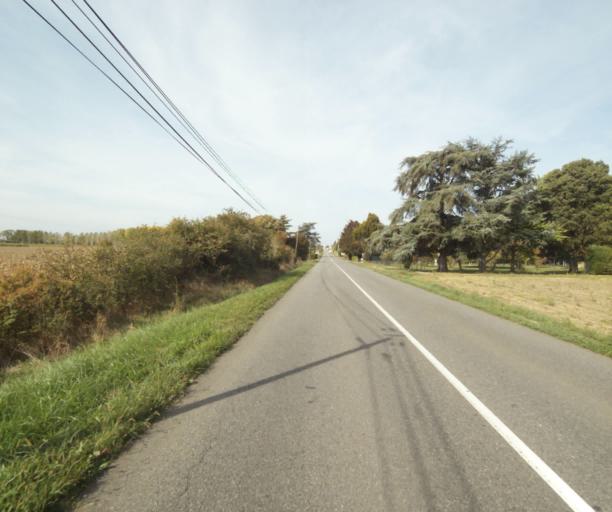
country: FR
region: Midi-Pyrenees
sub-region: Departement du Tarn-et-Garonne
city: Corbarieu
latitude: 43.9383
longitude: 1.3749
